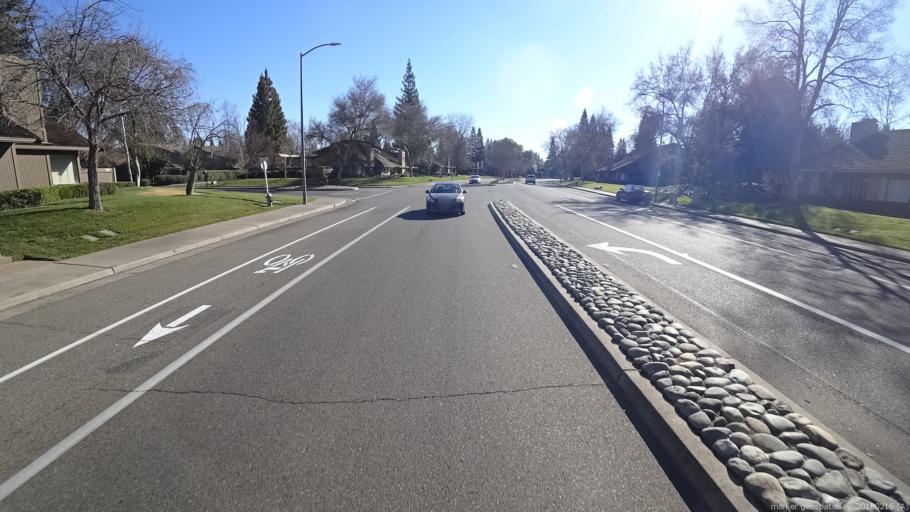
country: US
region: California
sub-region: Sacramento County
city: Gold River
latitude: 38.6325
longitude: -121.2559
